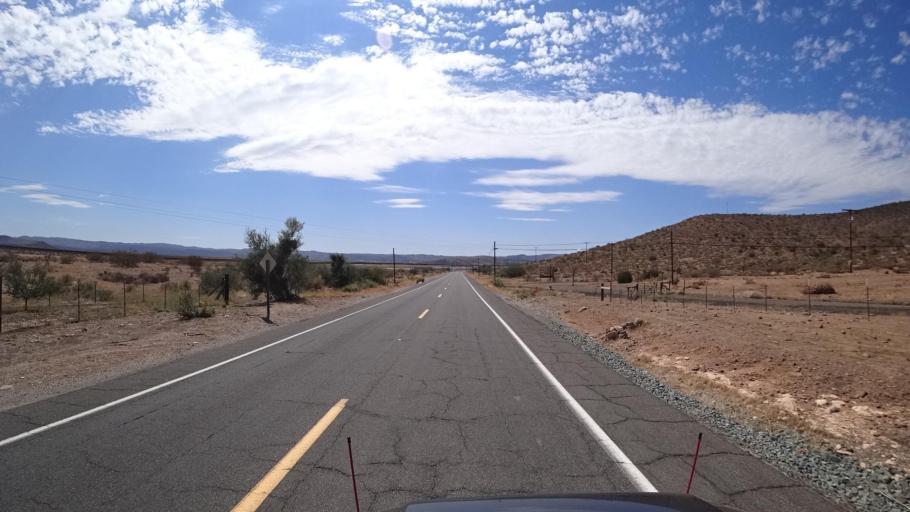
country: MX
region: Baja California
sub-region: Tecate
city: Cereso del Hongo
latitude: 32.6200
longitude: -116.1604
